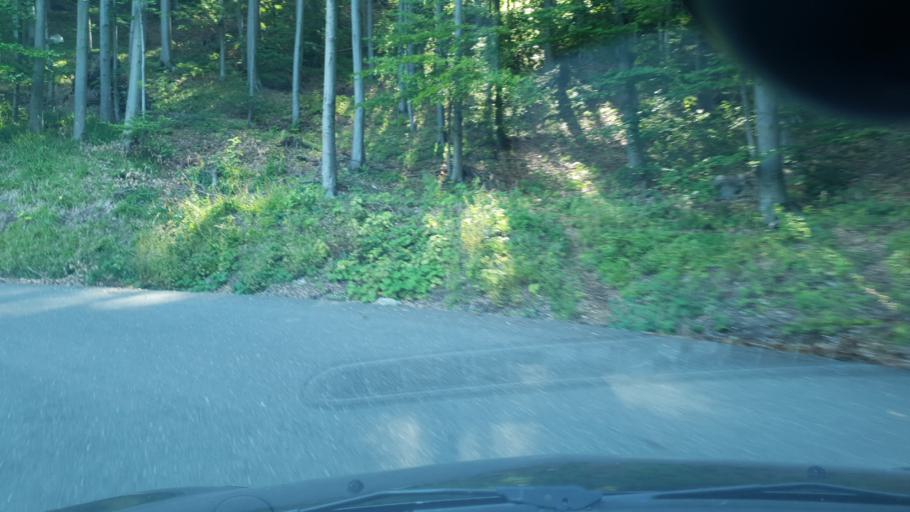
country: HR
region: Grad Zagreb
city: Kasina
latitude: 45.8865
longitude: 15.9712
